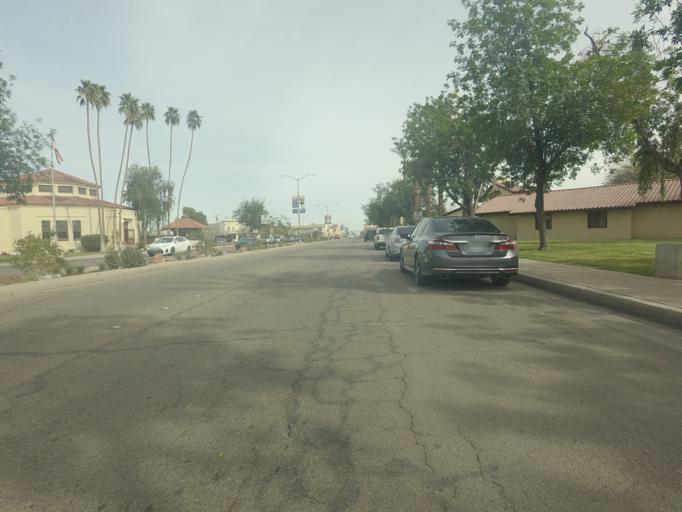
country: US
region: California
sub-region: Imperial County
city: Brawley
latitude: 32.9786
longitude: -115.5355
